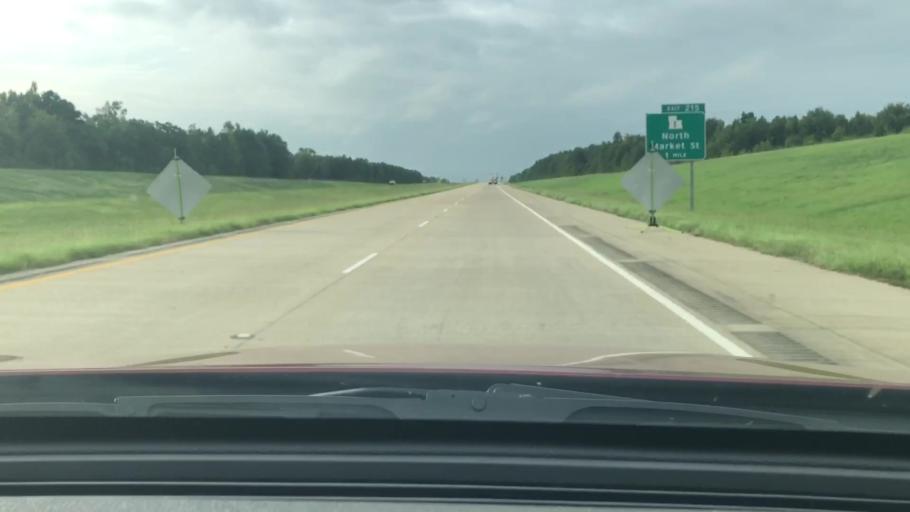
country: US
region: Louisiana
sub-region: Caddo Parish
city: Blanchard
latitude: 32.6159
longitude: -93.8353
